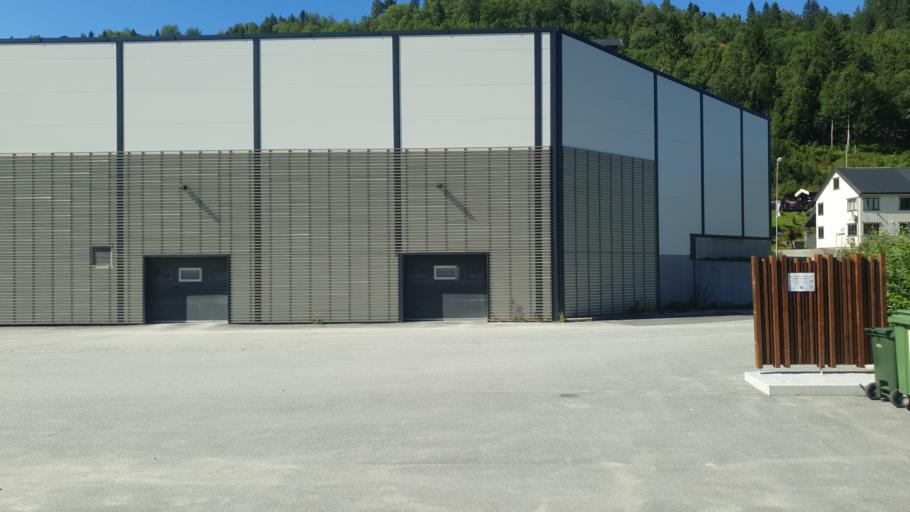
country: NO
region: Sor-Trondelag
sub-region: Meldal
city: Meldal
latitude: 63.1267
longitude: 9.7061
